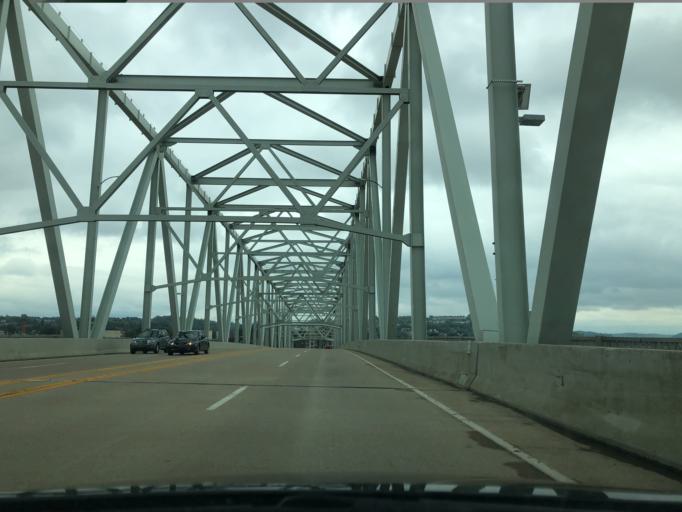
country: US
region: Kentucky
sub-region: Campbell County
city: Newport
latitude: 39.0966
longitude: -84.5019
